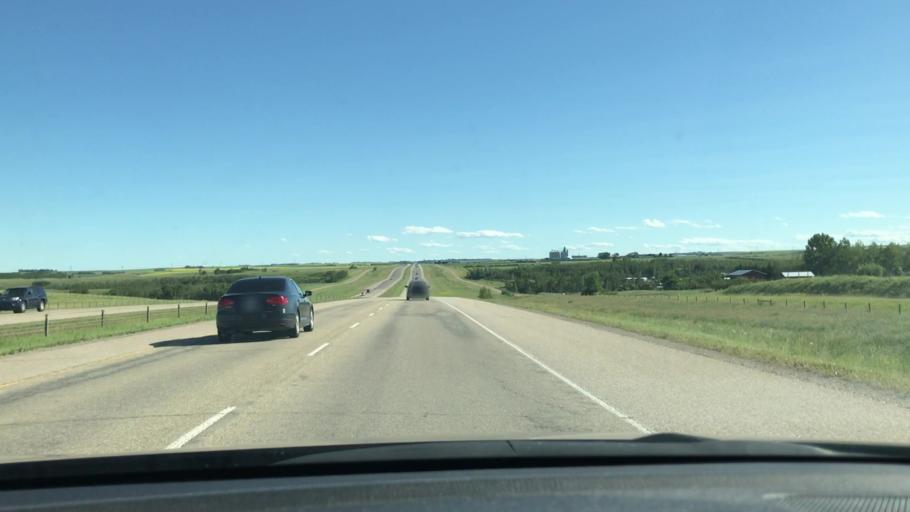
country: CA
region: Alberta
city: Carstairs
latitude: 51.5235
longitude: -114.0254
